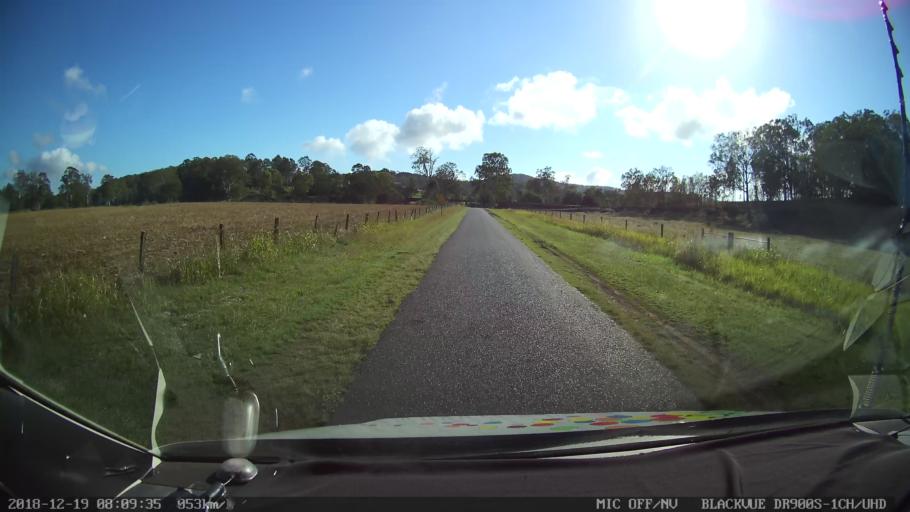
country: AU
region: Queensland
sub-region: Logan
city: Cedar Vale
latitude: -28.2138
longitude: 152.8799
